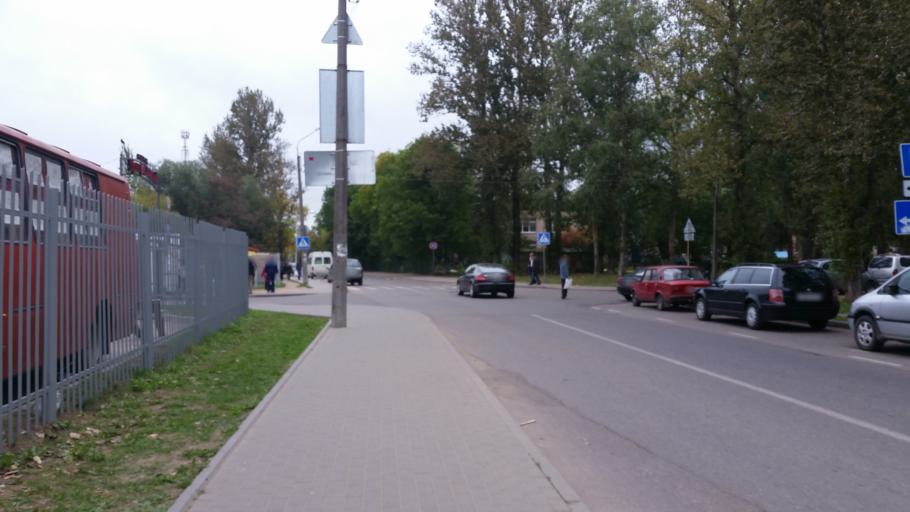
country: BY
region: Vitebsk
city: Vitebsk
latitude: 55.1805
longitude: 30.2239
